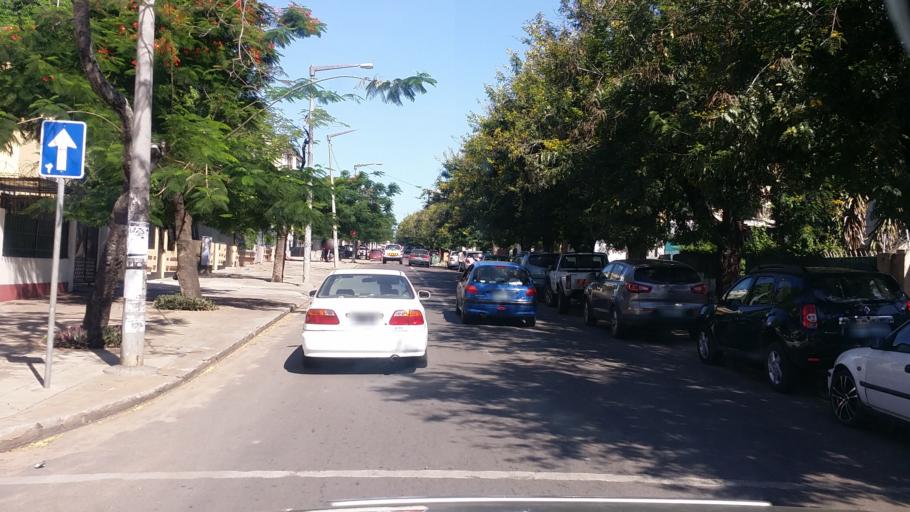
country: MZ
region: Maputo City
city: Maputo
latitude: -25.9609
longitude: 32.5789
